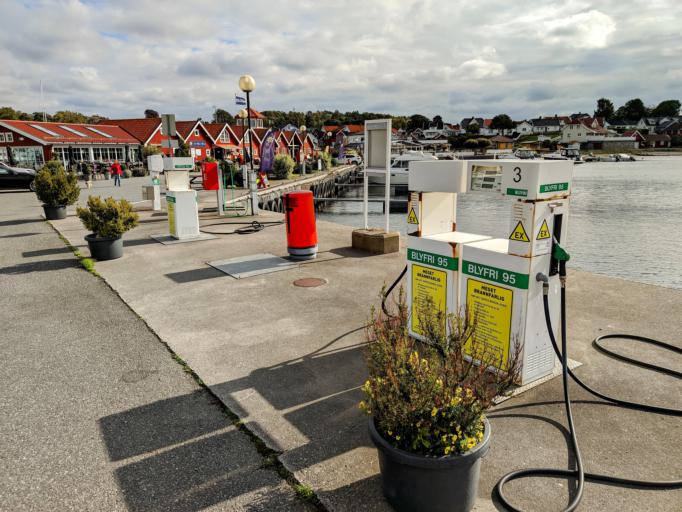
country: NO
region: Telemark
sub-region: Bamble
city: Langesund
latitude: 58.9942
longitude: 9.8559
